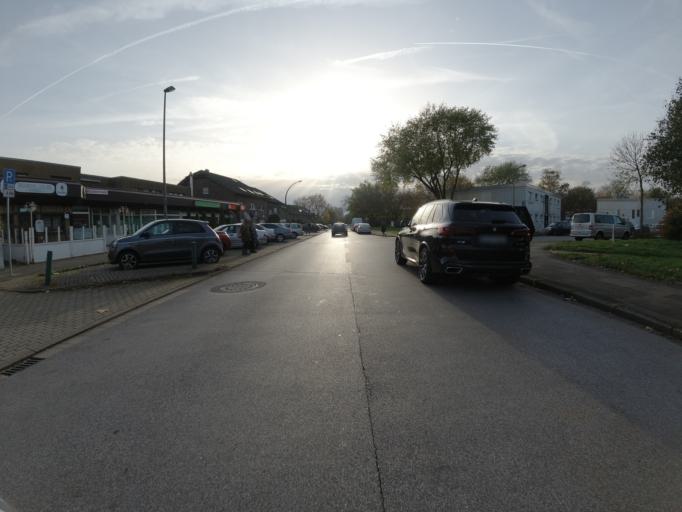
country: DE
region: North Rhine-Westphalia
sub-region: Regierungsbezirk Dusseldorf
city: Hochfeld
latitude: 51.3956
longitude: 6.7072
